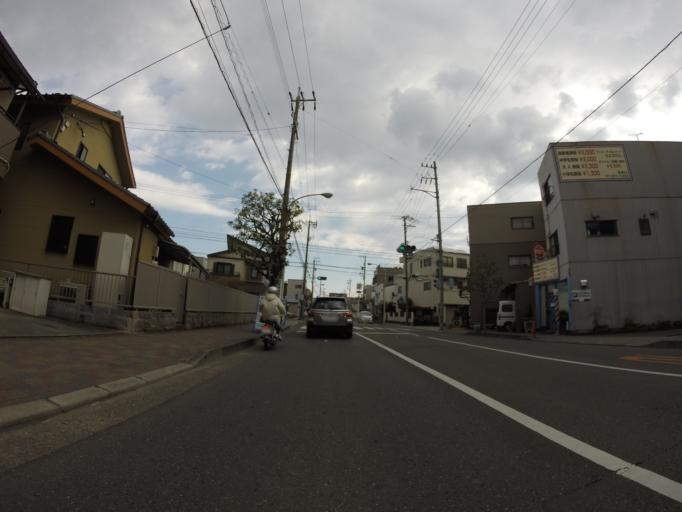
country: JP
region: Shizuoka
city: Shizuoka-shi
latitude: 34.9821
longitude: 138.3698
